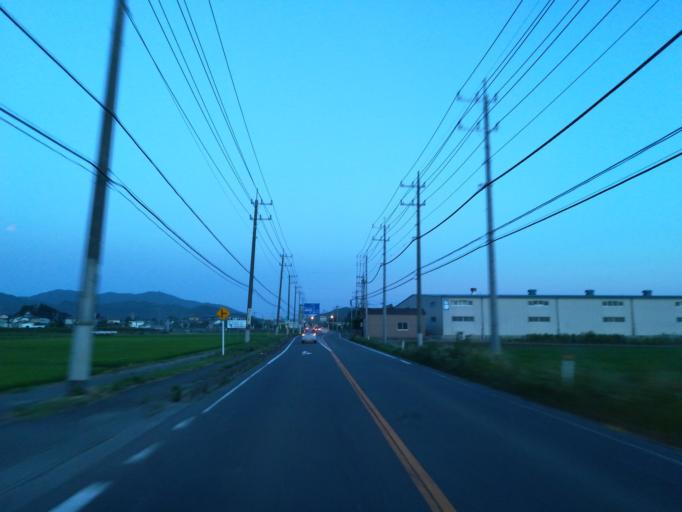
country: JP
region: Ibaraki
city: Tsukuba
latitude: 36.2094
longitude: 140.0724
